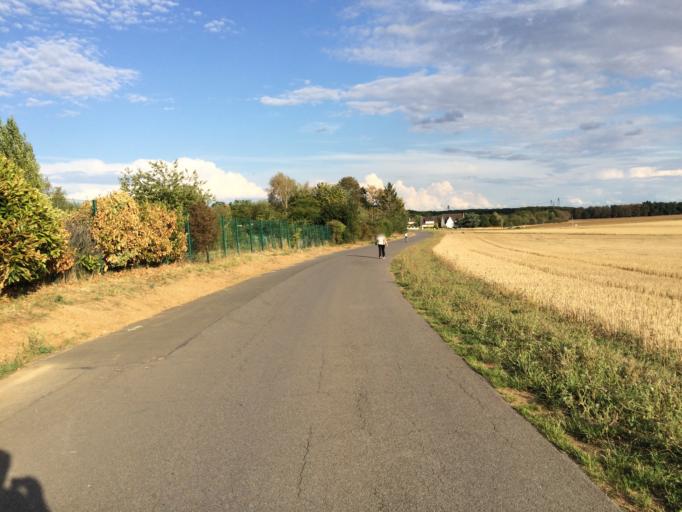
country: FR
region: Ile-de-France
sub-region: Departement de l'Essonne
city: Les Ulis
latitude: 48.6733
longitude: 2.1792
